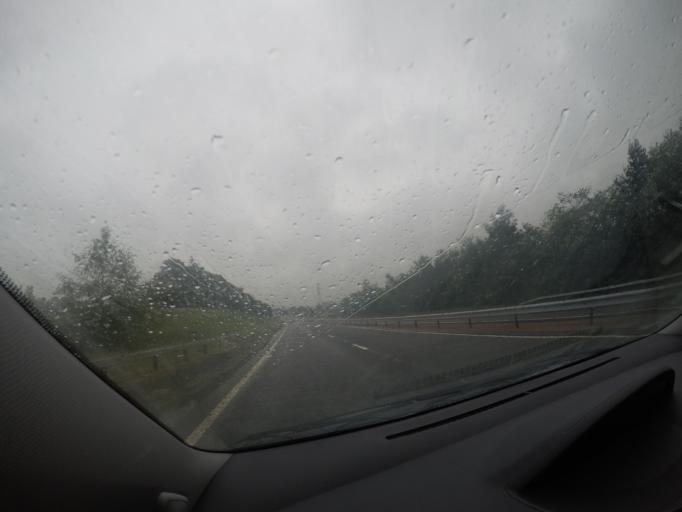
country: GB
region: Scotland
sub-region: Angus
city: Forfar
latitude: 56.5957
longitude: -2.9103
